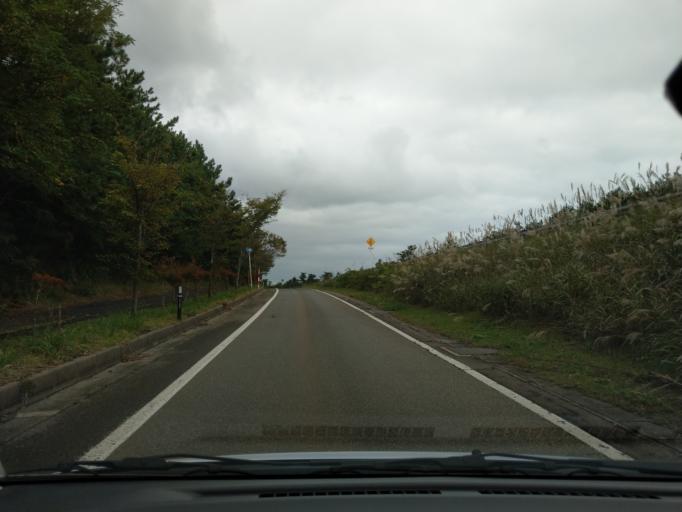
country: JP
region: Akita
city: Akita Shi
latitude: 39.6805
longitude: 140.0733
